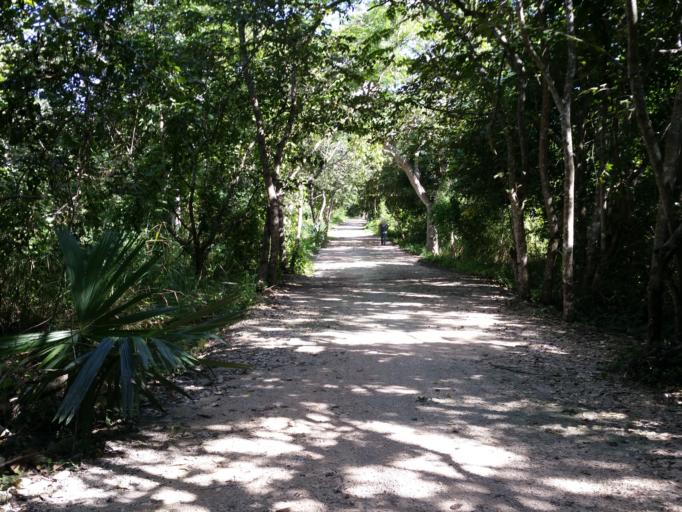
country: MX
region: Yucatan
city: Temozon
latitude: 20.8887
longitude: -88.1284
